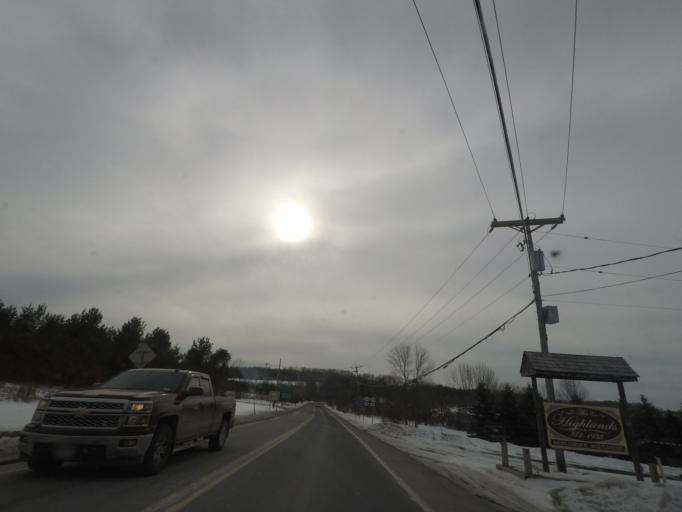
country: US
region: New York
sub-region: Albany County
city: Altamont
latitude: 42.6781
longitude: -74.0773
